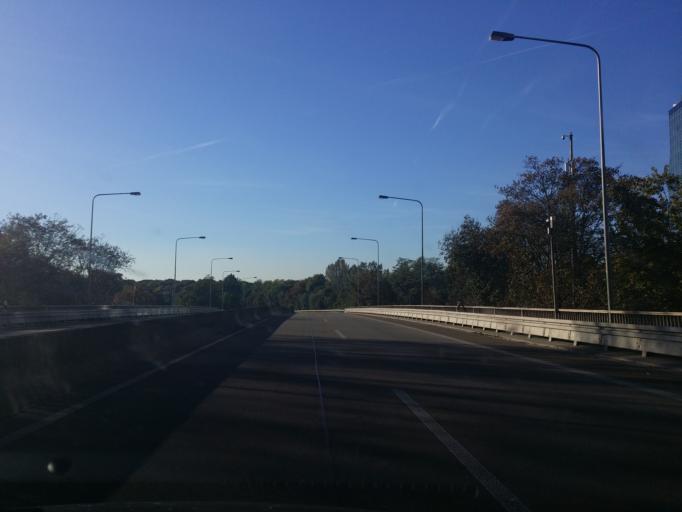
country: DE
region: Hesse
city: Niederrad
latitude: 50.1159
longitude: 8.6289
